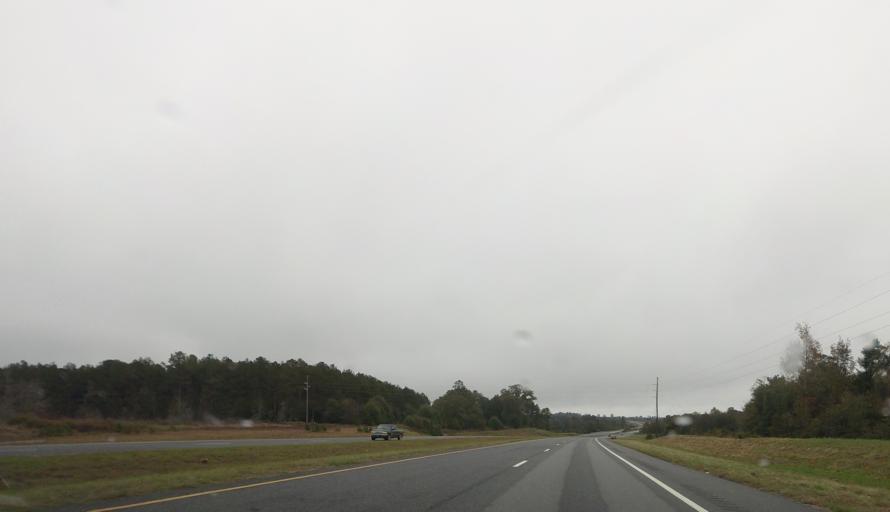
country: US
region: Georgia
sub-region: Taylor County
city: Reynolds
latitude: 32.5458
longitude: -84.0052
